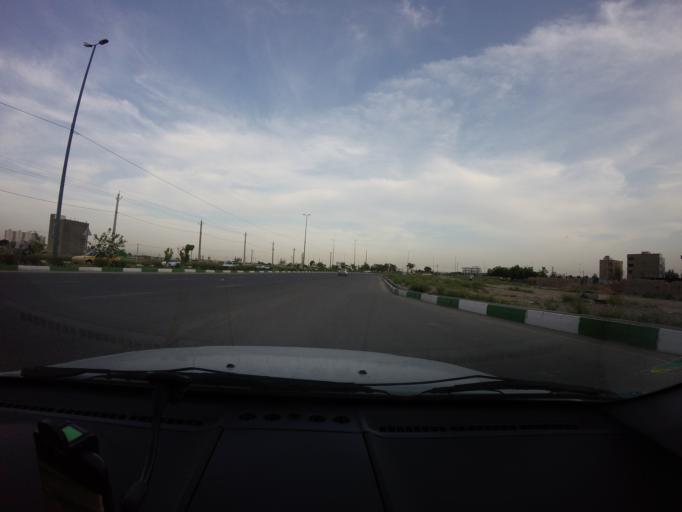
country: IR
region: Tehran
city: Eslamshahr
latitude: 35.5341
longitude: 51.2319
